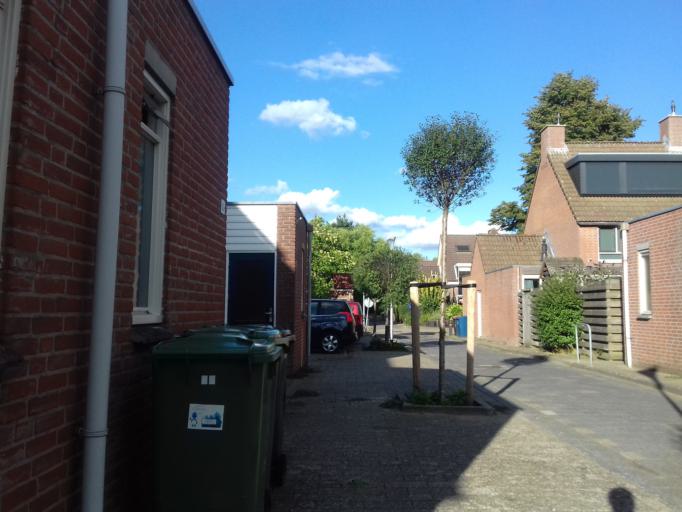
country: NL
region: Utrecht
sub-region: Gemeente Houten
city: Houten
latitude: 52.0377
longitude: 5.1577
